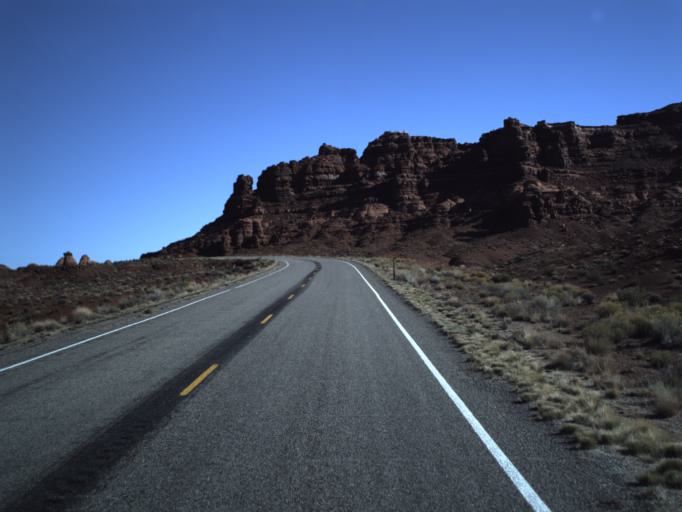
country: US
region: Utah
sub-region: San Juan County
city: Blanding
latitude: 37.8645
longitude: -110.3448
